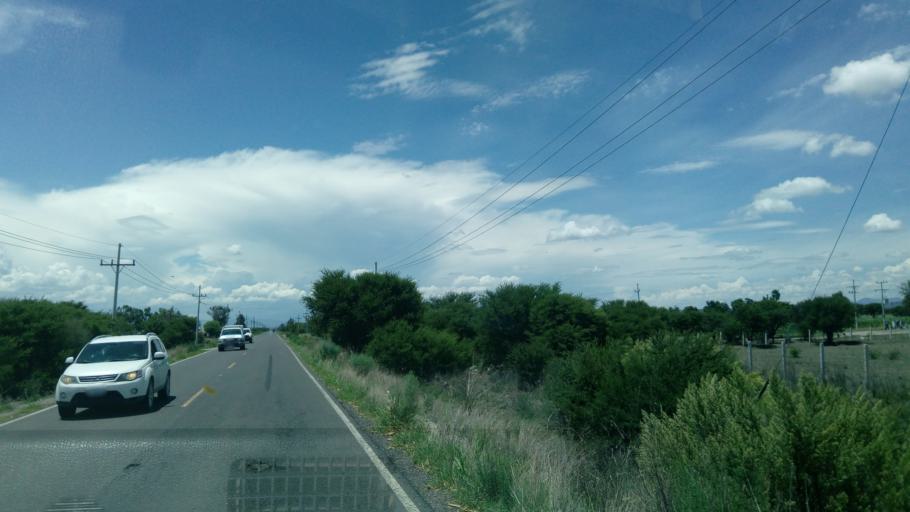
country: MX
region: Durango
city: Victoria de Durango
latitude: 24.1643
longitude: -104.5269
